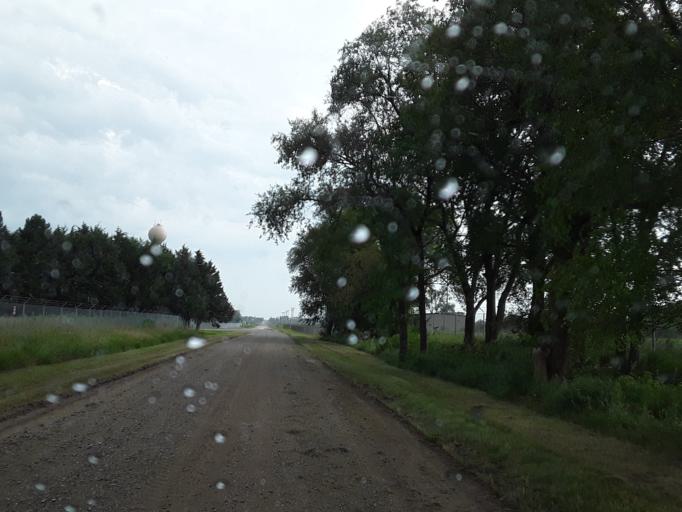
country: US
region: Nebraska
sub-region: Saunders County
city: Yutan
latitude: 41.1890
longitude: -96.4450
